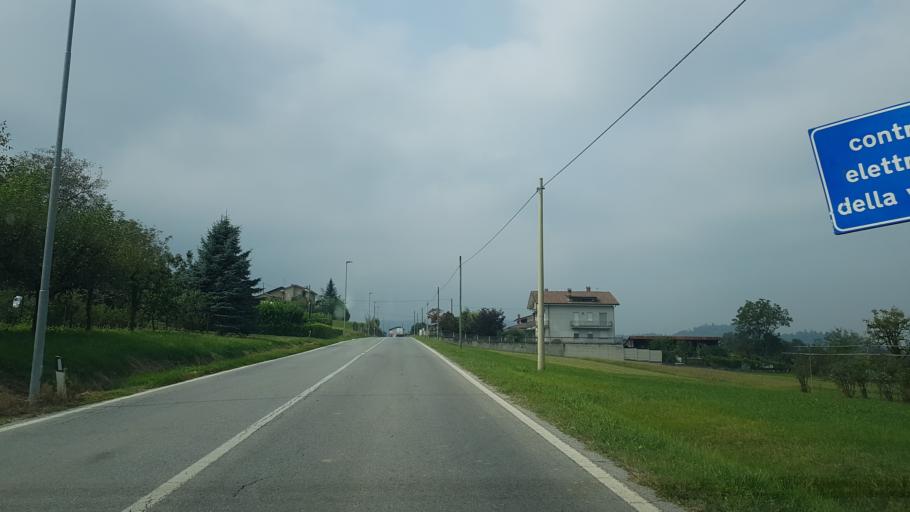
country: IT
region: Piedmont
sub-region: Provincia di Cuneo
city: Chiusa di Pesio
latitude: 44.3281
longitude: 7.6518
